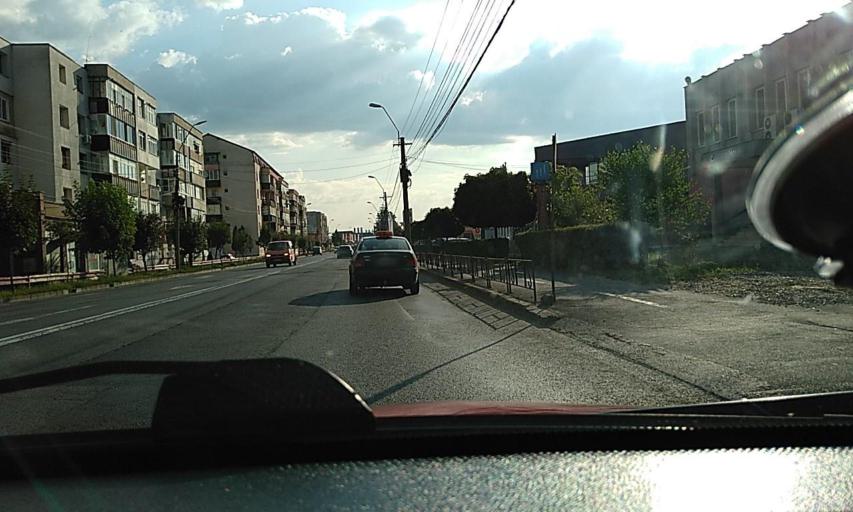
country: RO
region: Mures
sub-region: Comuna Albesti
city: Albesti
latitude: 46.2307
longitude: 24.8208
